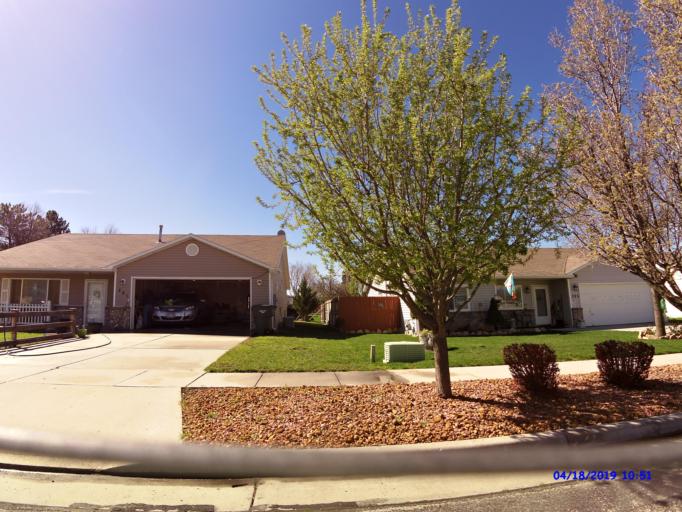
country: US
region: Utah
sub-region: Weber County
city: North Ogden
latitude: 41.2834
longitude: -111.9607
